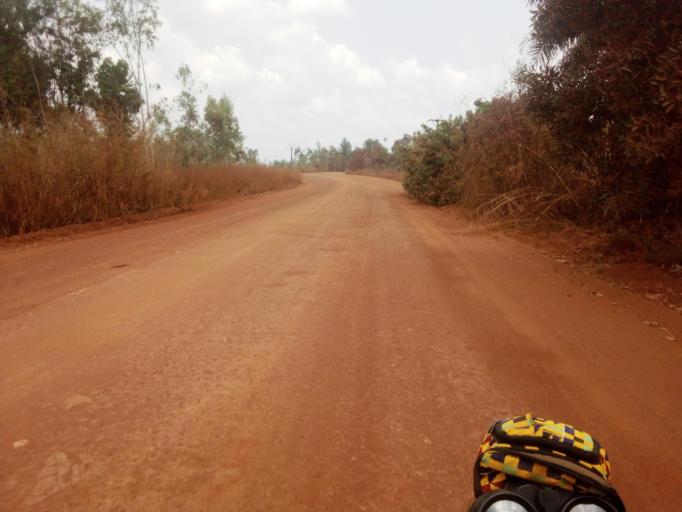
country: SL
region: Southern Province
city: Mogbwemo
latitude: 7.7529
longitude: -12.2938
